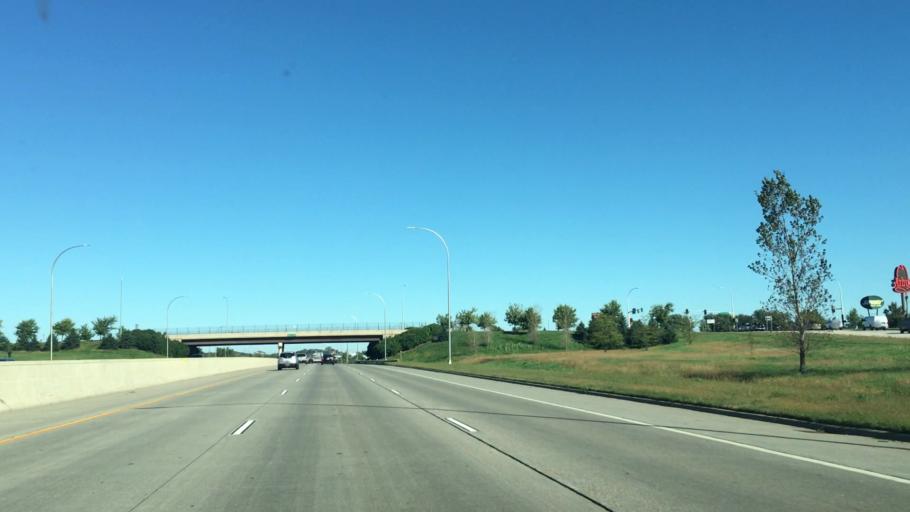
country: US
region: Minnesota
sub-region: Olmsted County
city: Rochester
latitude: 44.0595
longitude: -92.4969
